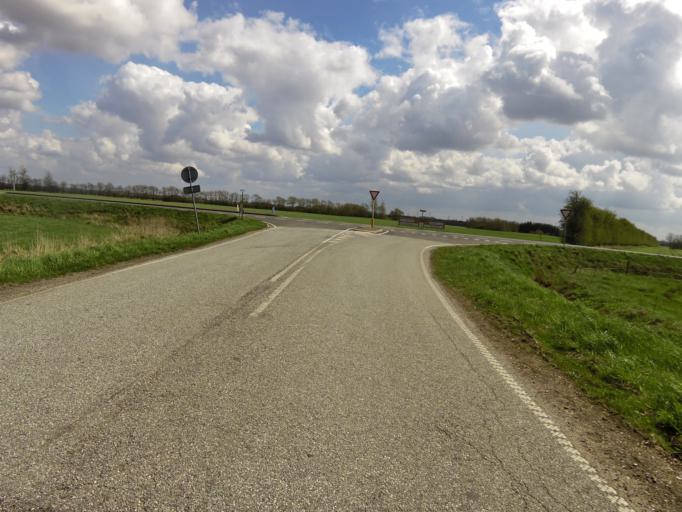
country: DK
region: South Denmark
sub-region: Tonder Kommune
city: Toftlund
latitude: 55.2092
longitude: 9.0934
